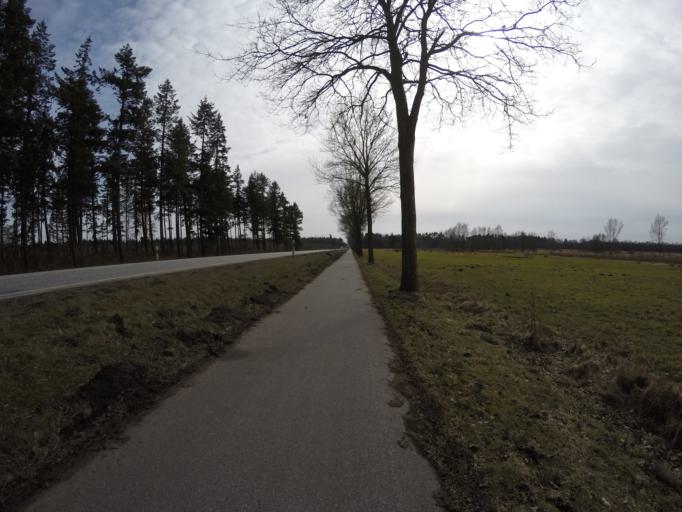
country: DE
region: Schleswig-Holstein
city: Lentfohrden
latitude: 53.8394
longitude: 9.8853
